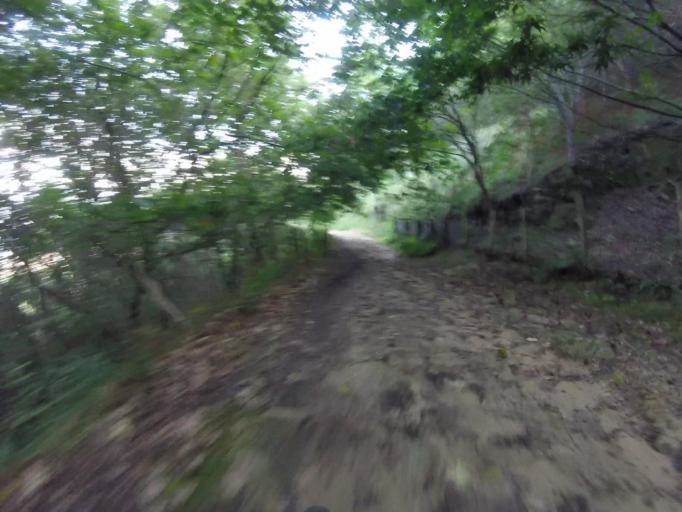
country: ES
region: Basque Country
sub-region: Provincia de Guipuzcoa
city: Fuenterrabia
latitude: 43.3542
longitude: -1.8377
